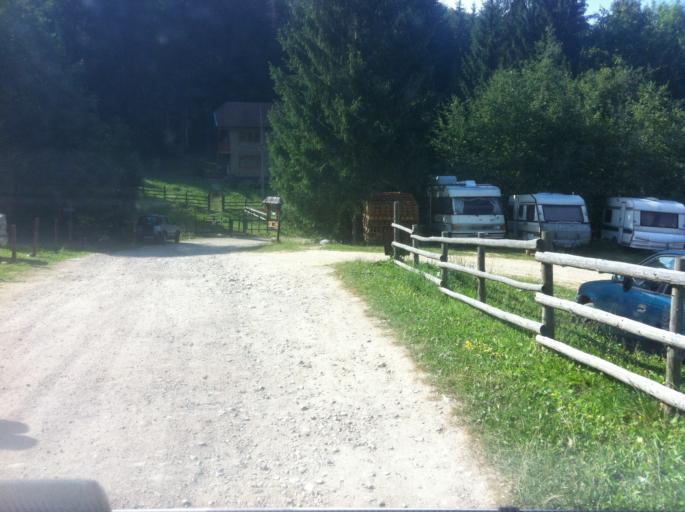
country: RO
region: Hunedoara
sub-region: Comuna Rau de Mori
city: Rau de Mori
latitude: 45.4343
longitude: 22.8932
